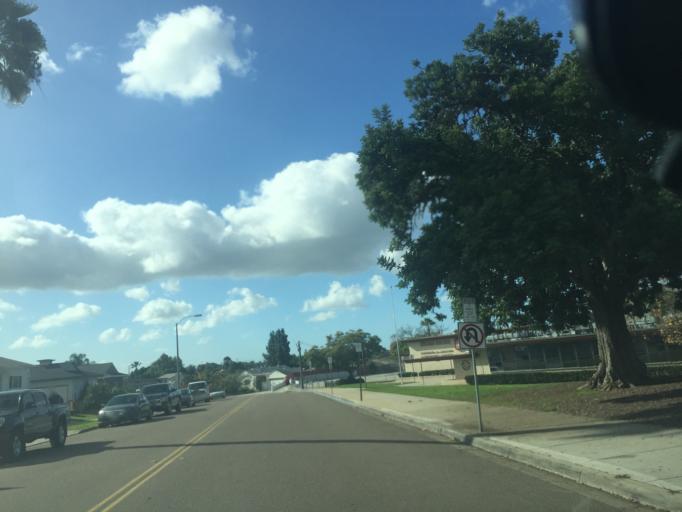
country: US
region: California
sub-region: San Diego County
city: La Mesa
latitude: 32.7924
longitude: -117.0836
